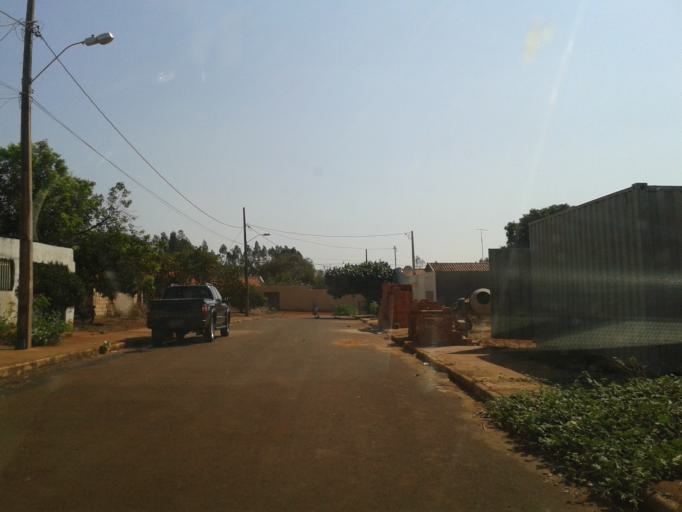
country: BR
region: Minas Gerais
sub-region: Ituiutaba
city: Ituiutaba
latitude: -18.9580
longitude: -49.4802
